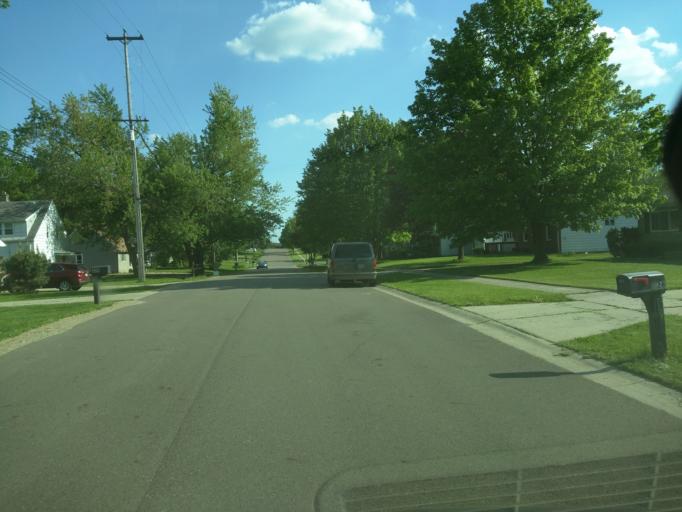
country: US
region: Michigan
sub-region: Eaton County
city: Waverly
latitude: 42.7304
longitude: -84.6055
